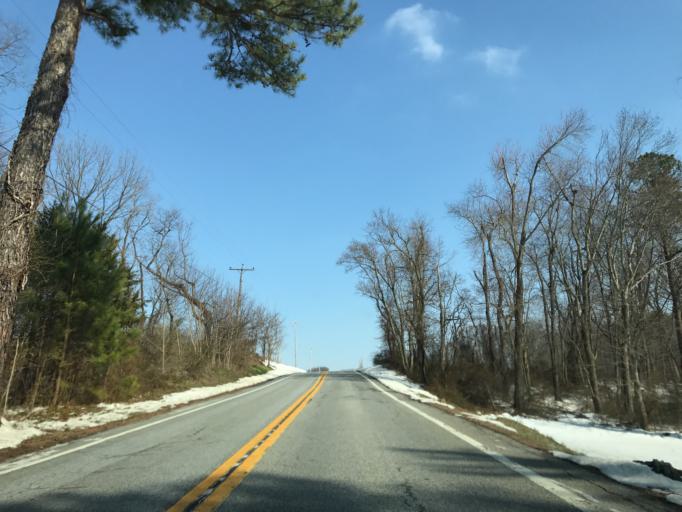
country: US
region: Maryland
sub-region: Harford County
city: Jarrettsville
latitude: 39.7034
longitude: -76.4993
